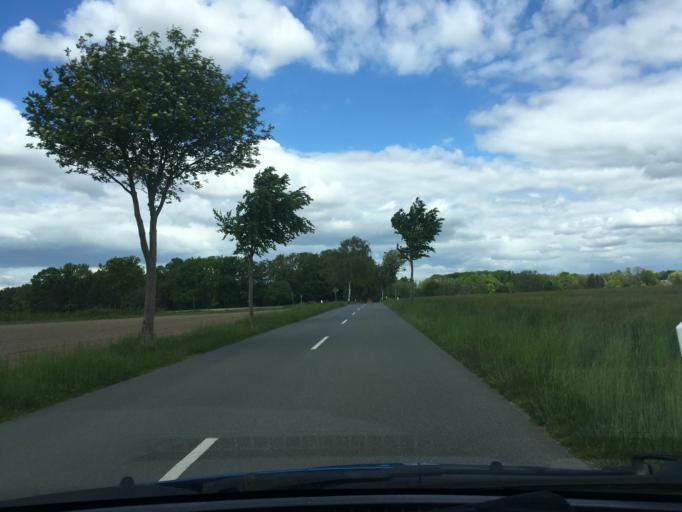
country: DE
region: Lower Saxony
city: Suderburg
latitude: 52.9212
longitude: 10.4386
